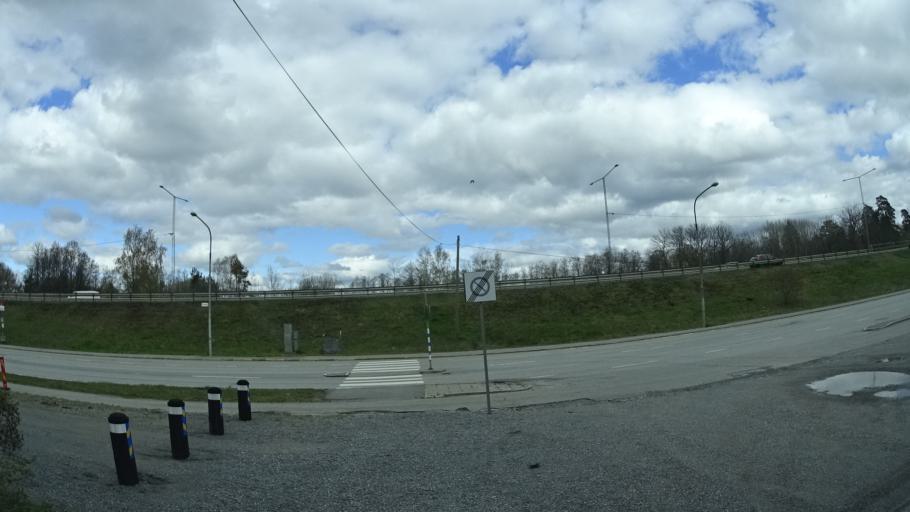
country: SE
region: Stockholm
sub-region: Nacka Kommun
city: Alta
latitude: 59.2604
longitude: 18.1581
